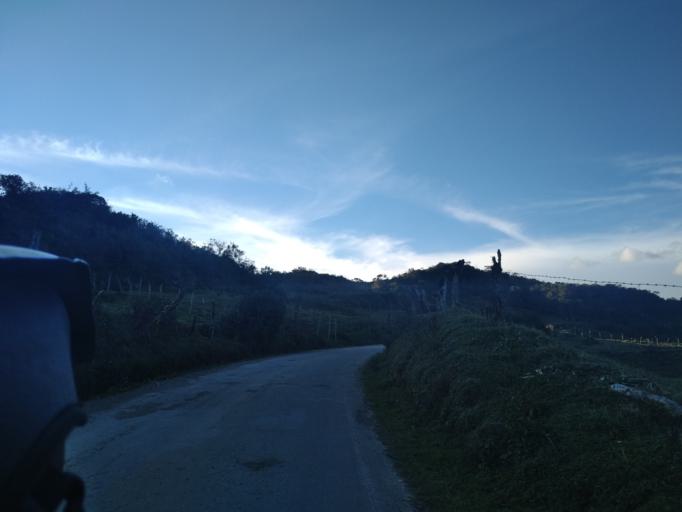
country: PE
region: Amazonas
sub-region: Provincia de Chachapoyas
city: Montevideo
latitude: -6.7130
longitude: -77.8663
